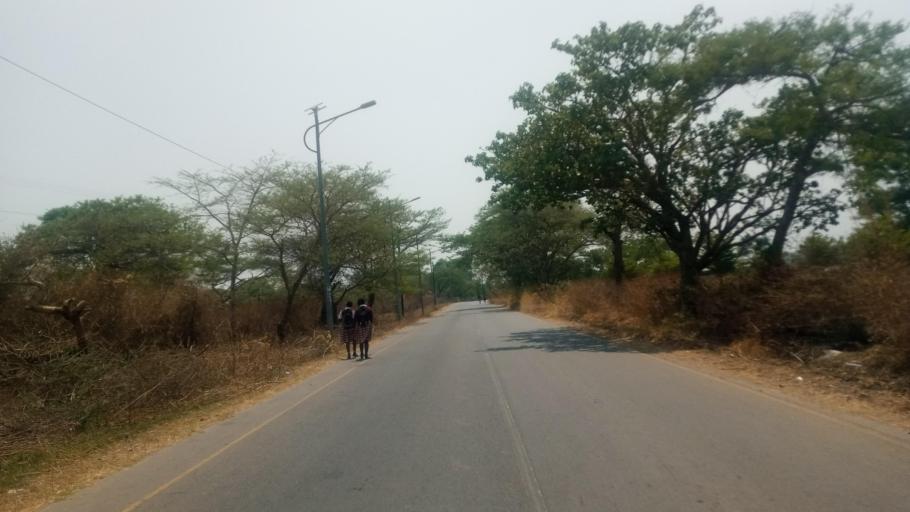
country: ZM
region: Lusaka
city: Lusaka
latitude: -15.4582
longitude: 28.4369
